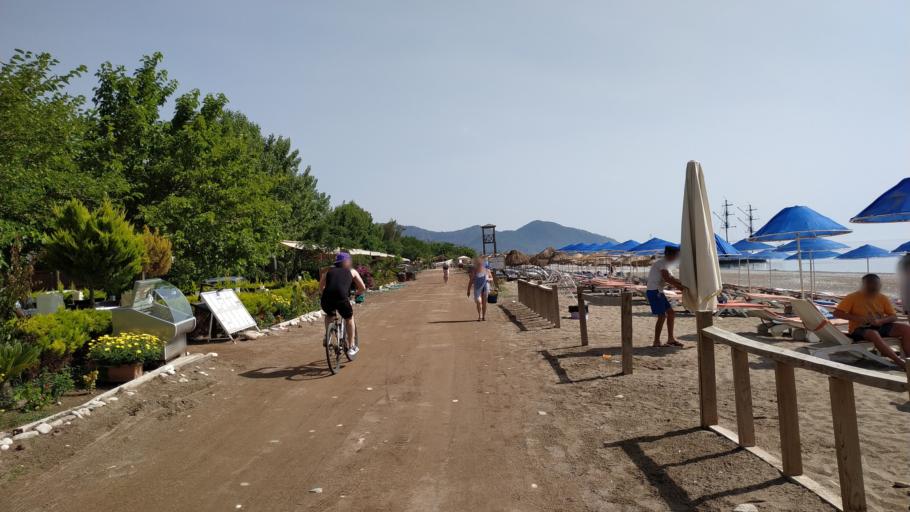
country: TR
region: Antalya
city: Tekirova
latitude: 36.4034
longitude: 30.4774
